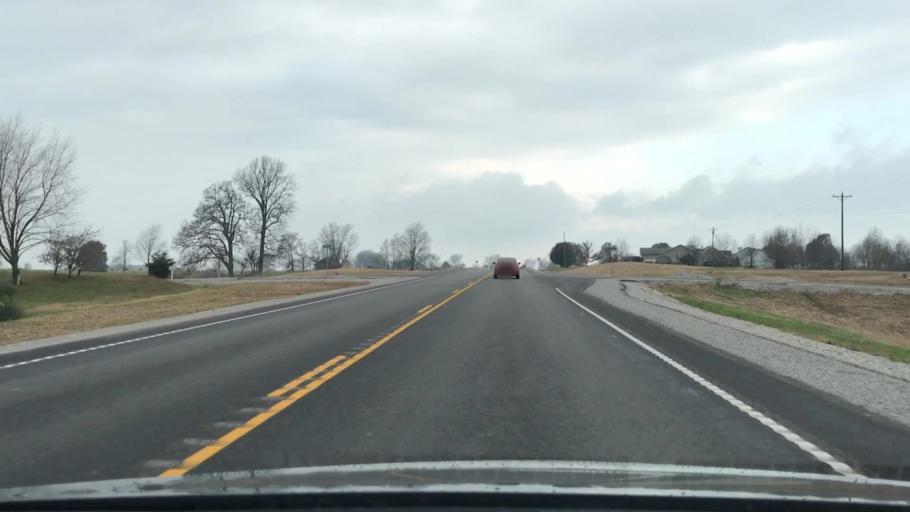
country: US
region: Kentucky
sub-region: Simpson County
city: Franklin
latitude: 36.7094
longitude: -86.4930
